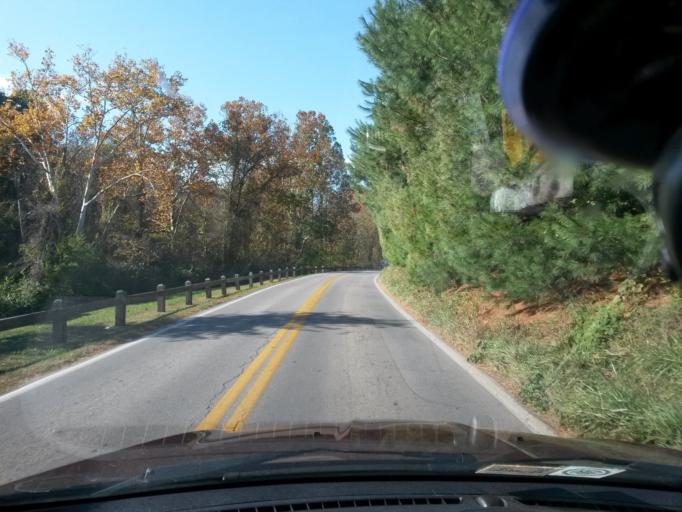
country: US
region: Virginia
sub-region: Roanoke County
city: Vinton
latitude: 37.2942
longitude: -79.9204
